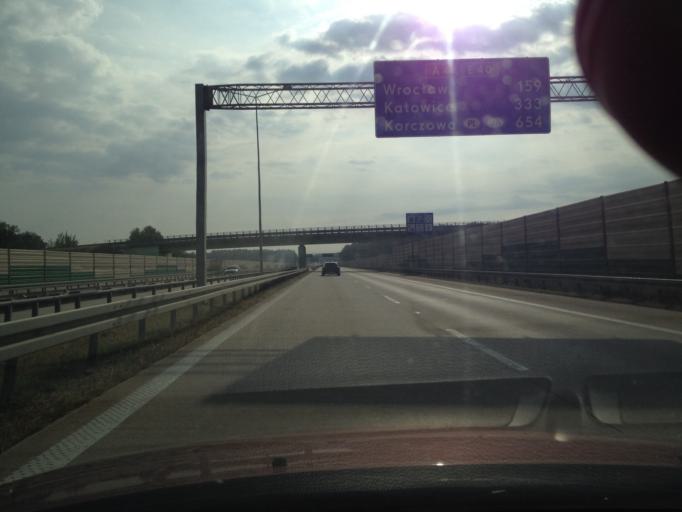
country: PL
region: Lower Silesian Voivodeship
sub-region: Powiat zgorzelecki
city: Lagow
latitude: 51.1713
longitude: 15.0414
